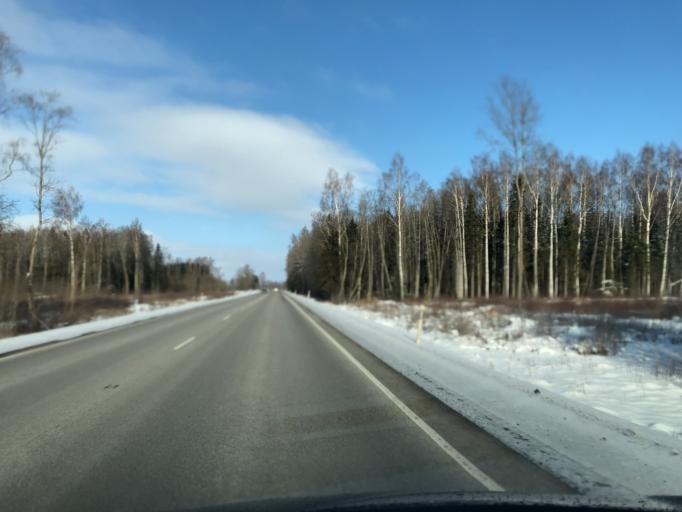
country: EE
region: Jaervamaa
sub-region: Paide linn
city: Paide
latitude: 58.8104
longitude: 25.7577
